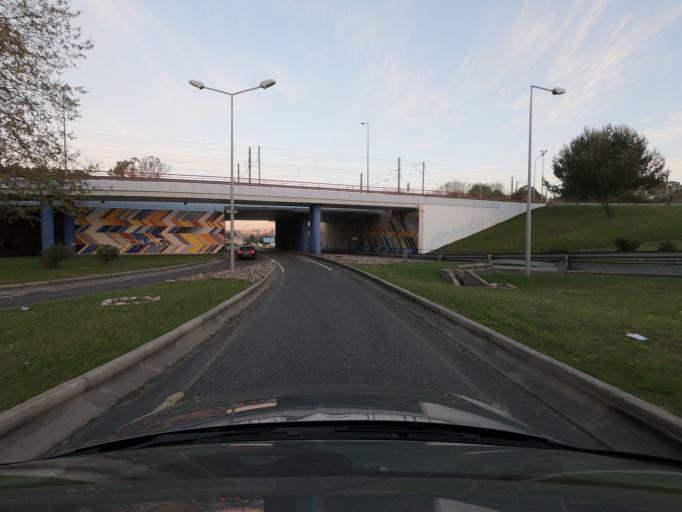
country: PT
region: Lisbon
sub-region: Sintra
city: Queluz
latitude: 38.7542
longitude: -9.2668
